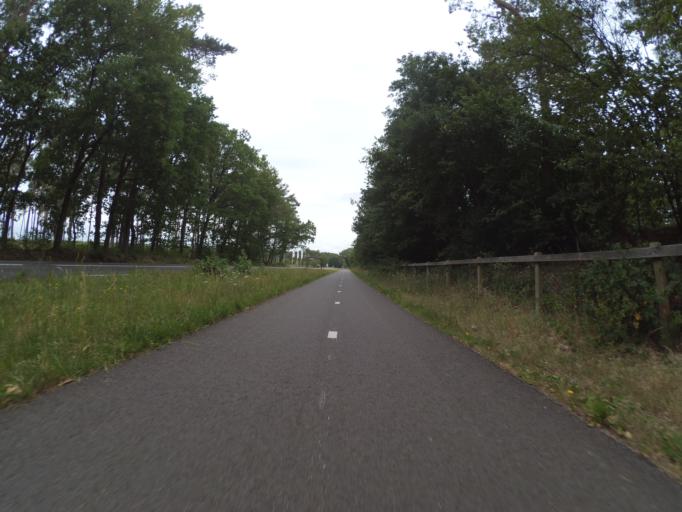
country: NL
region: Gelderland
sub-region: Gemeente Ede
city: Otterlo
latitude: 52.0867
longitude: 5.7770
